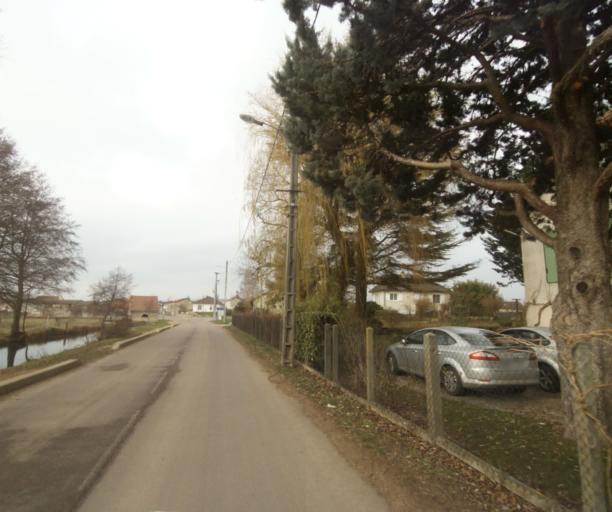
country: FR
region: Champagne-Ardenne
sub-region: Departement de la Haute-Marne
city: Villiers-en-Lieu
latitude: 48.6504
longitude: 4.8180
